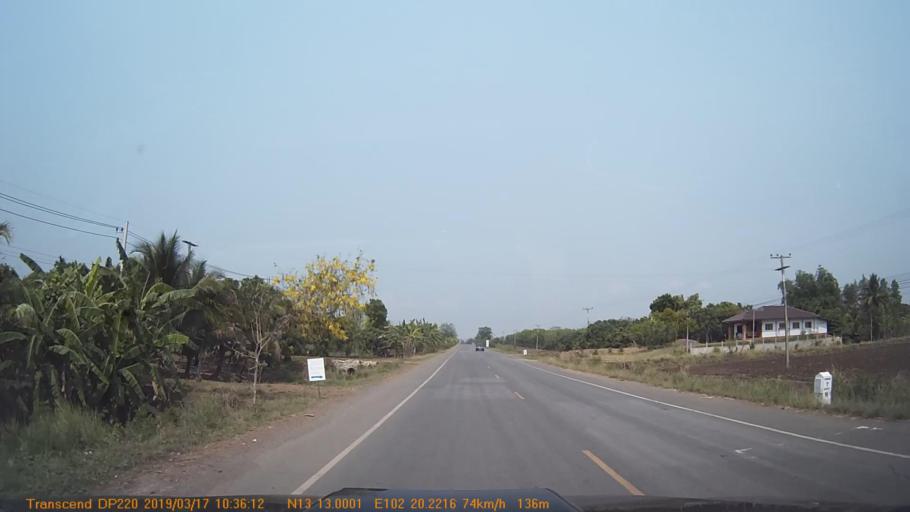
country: TH
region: Chanthaburi
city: Soi Dao
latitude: 13.2168
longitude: 102.3367
